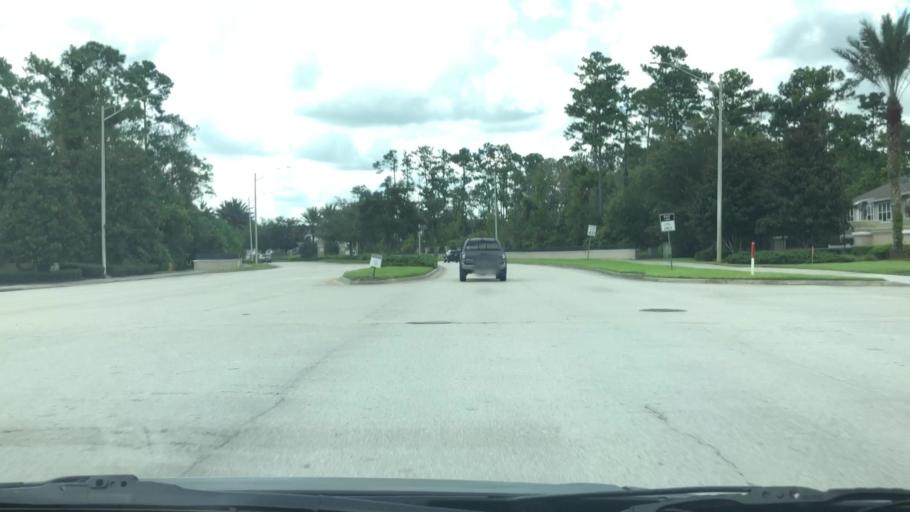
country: US
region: Florida
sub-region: Saint Johns County
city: Fruit Cove
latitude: 30.1240
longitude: -81.5309
